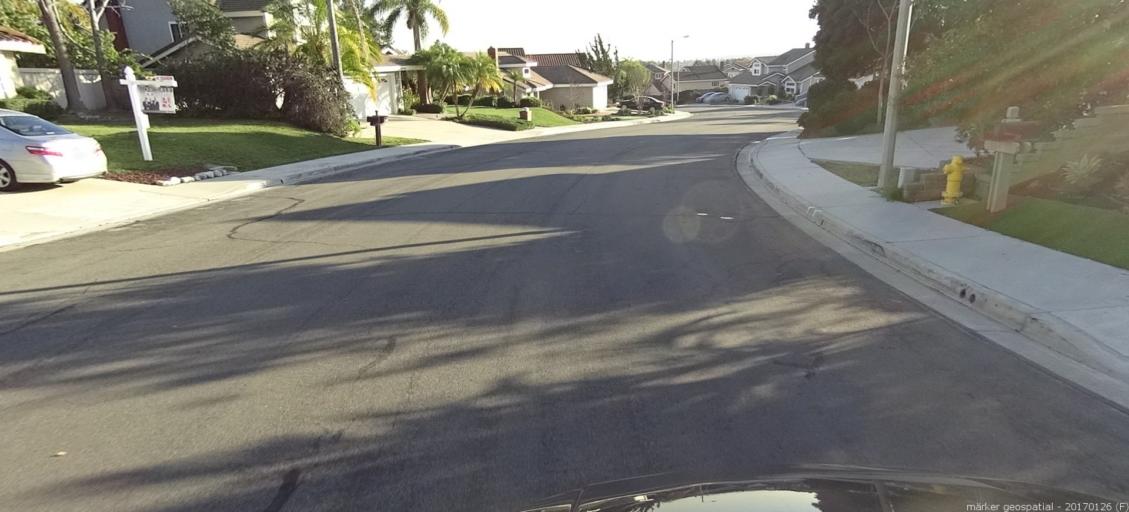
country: US
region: California
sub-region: Orange County
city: Lake Forest
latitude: 33.6476
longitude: -117.6728
